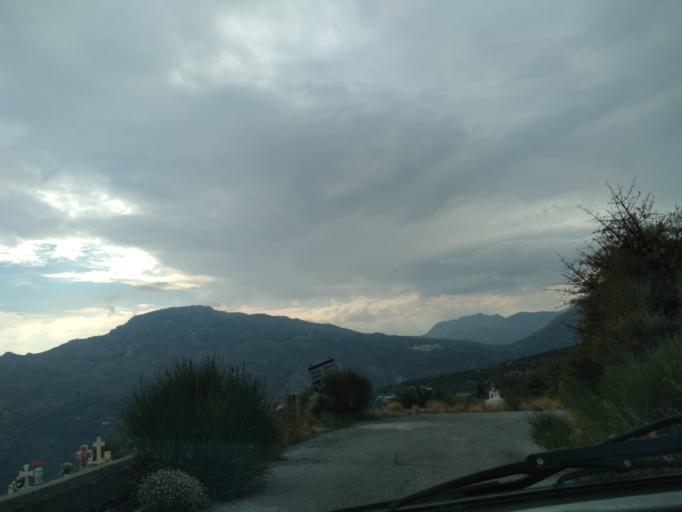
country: GR
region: Crete
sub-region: Nomos Lasithiou
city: Makry-Gialos
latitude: 35.1222
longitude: 26.0211
